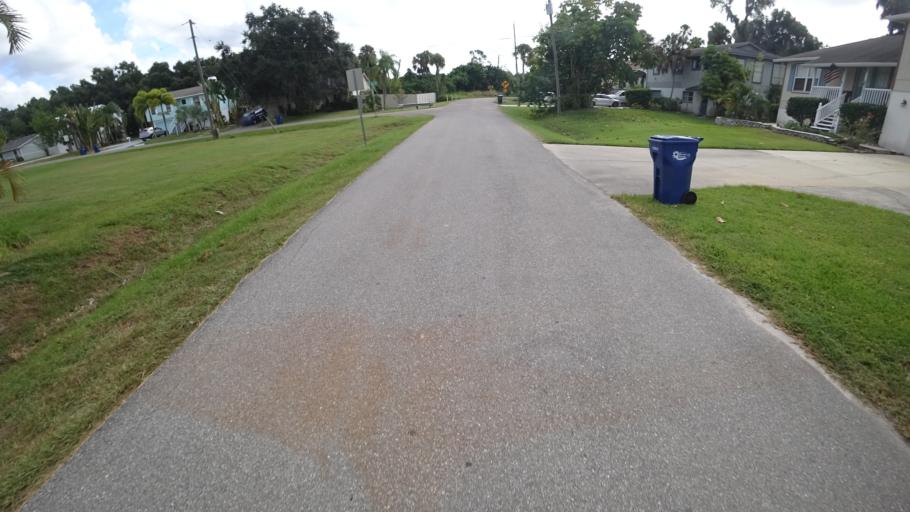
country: US
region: Florida
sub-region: Manatee County
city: Memphis
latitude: 27.5472
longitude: -82.5695
